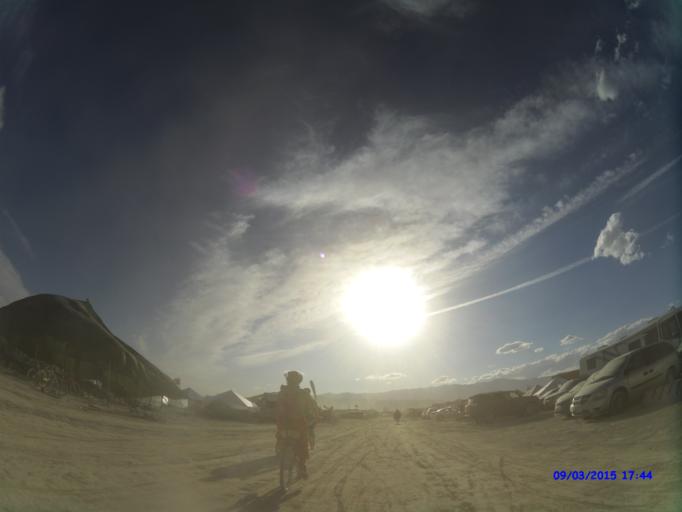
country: US
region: Nevada
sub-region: Pershing County
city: Lovelock
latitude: 40.7752
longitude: -119.2043
